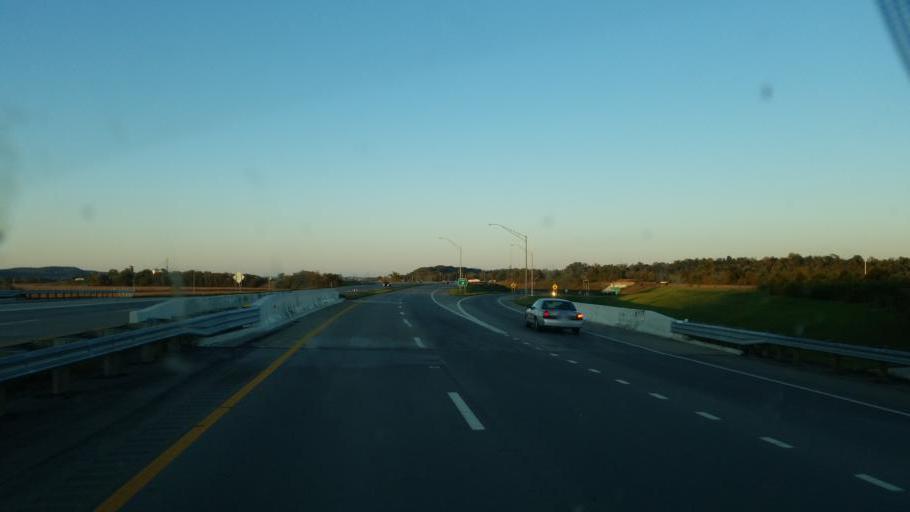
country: US
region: Ohio
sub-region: Pike County
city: Piketon
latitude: 39.0448
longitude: -83.0263
